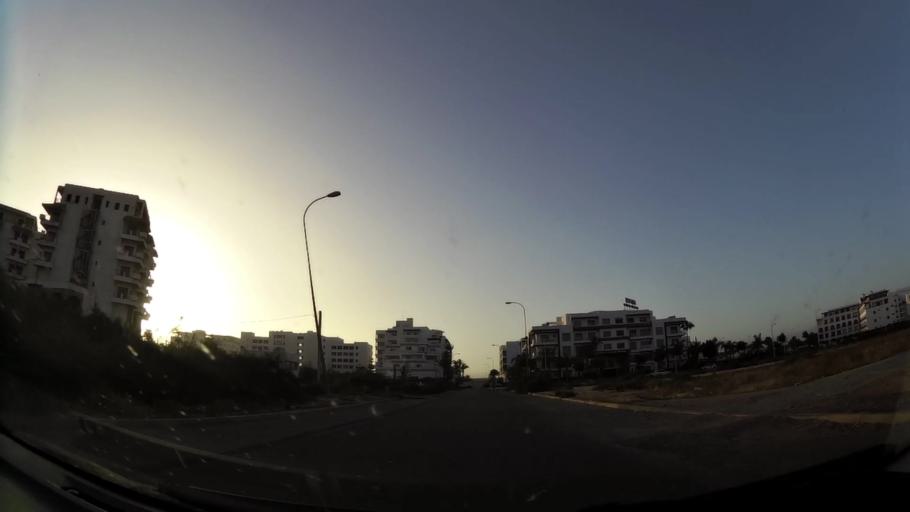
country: MA
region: Souss-Massa-Draa
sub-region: Agadir-Ida-ou-Tnan
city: Agadir
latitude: 30.3993
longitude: -9.5899
